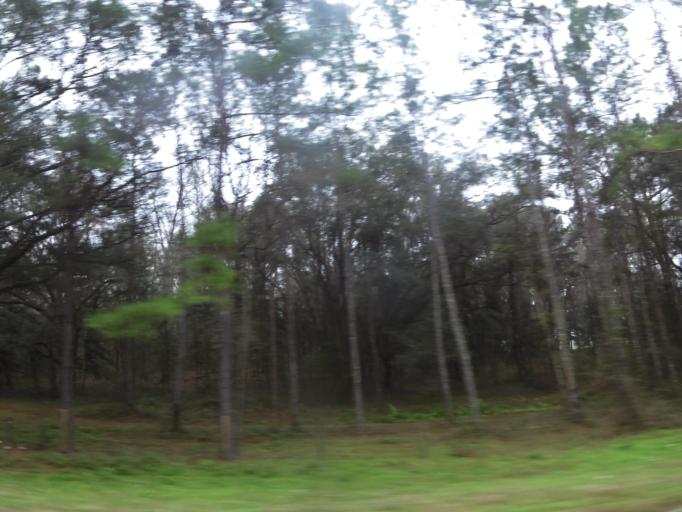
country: US
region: Florida
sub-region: Alachua County
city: Alachua
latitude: 29.8949
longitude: -82.4484
